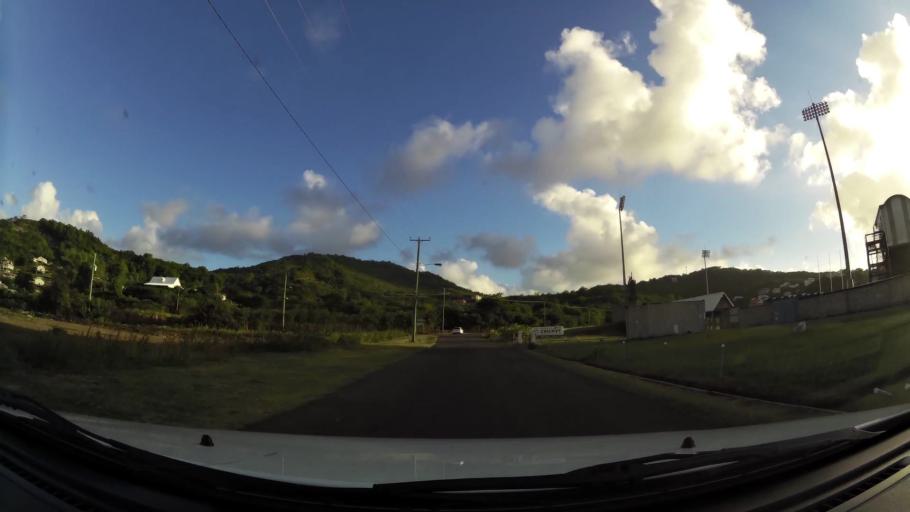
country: LC
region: Gros-Islet
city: Gros Islet
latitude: 14.0718
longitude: -60.9306
